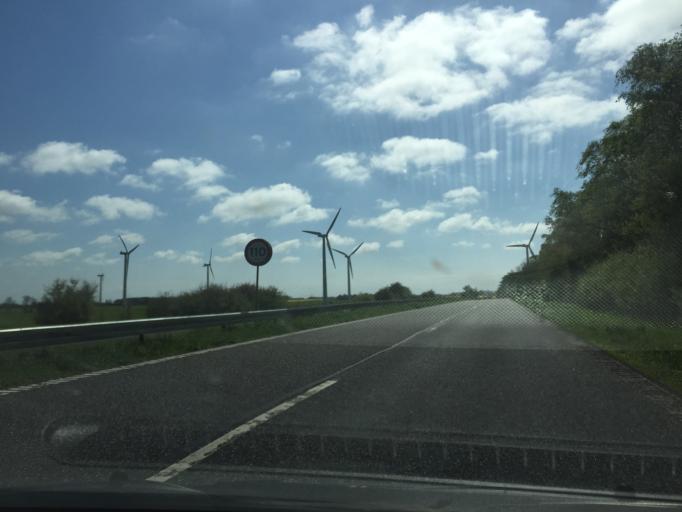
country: DK
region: Zealand
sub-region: Lolland Kommune
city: Holeby
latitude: 54.7435
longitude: 11.4490
